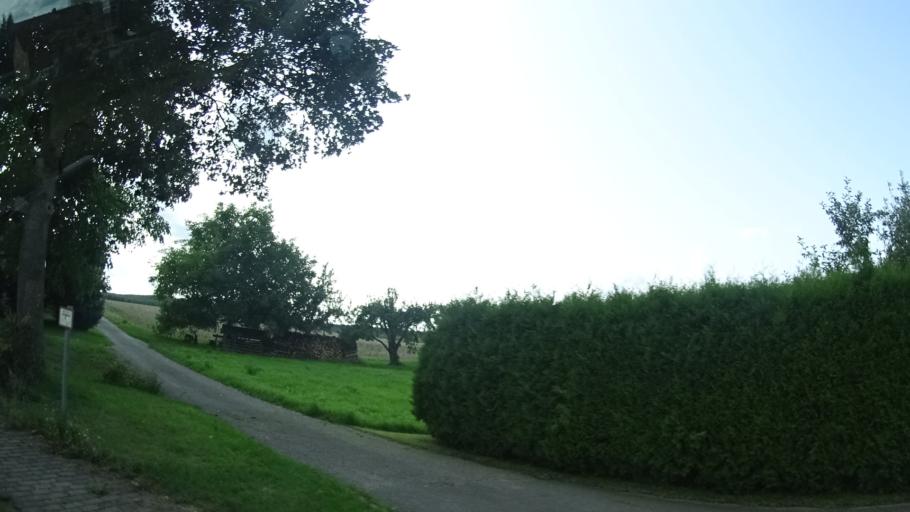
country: DE
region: Baden-Wuerttemberg
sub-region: Regierungsbezirk Stuttgart
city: Werbach
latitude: 49.7121
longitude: 9.6070
